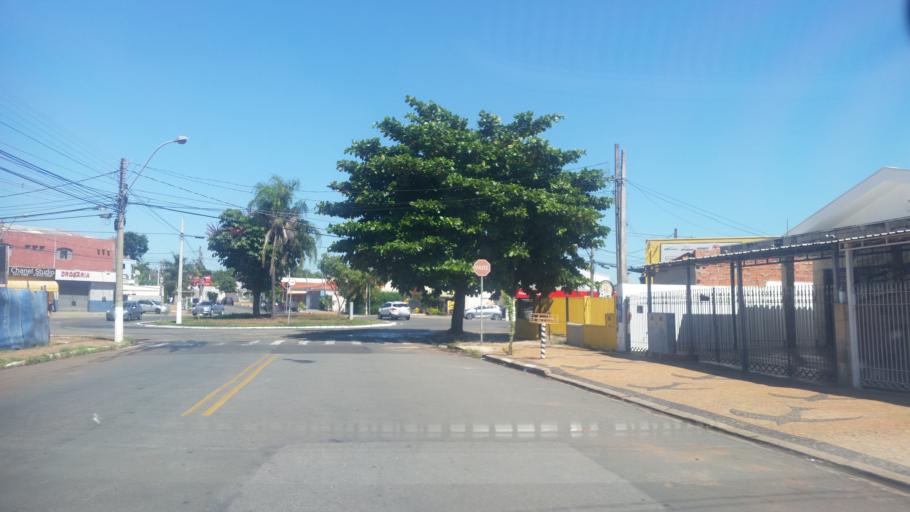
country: BR
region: Sao Paulo
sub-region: Campinas
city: Campinas
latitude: -22.8697
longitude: -47.0631
